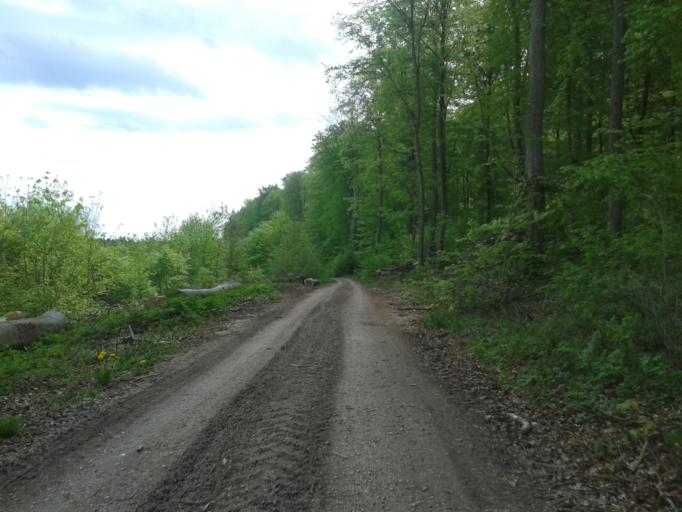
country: DE
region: Baden-Wuerttemberg
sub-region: Tuebingen Region
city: Blaubeuren
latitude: 48.3784
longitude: 9.8212
